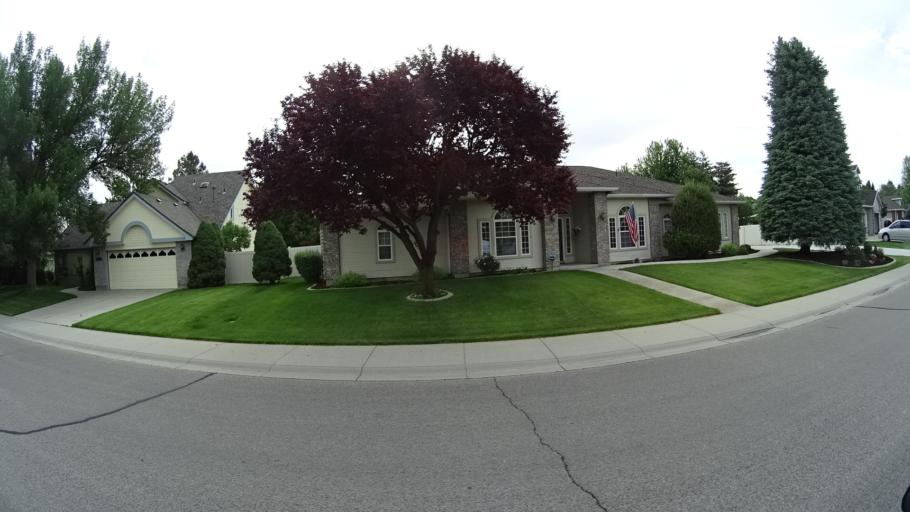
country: US
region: Idaho
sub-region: Ada County
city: Meridian
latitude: 43.5879
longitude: -116.3856
